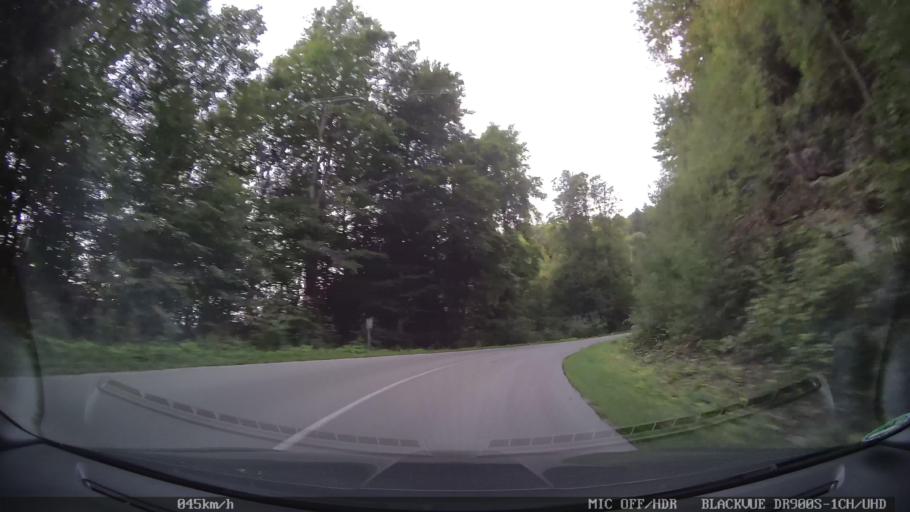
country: HR
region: Primorsko-Goranska
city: Vrbovsko
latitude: 45.2023
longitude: 15.0264
